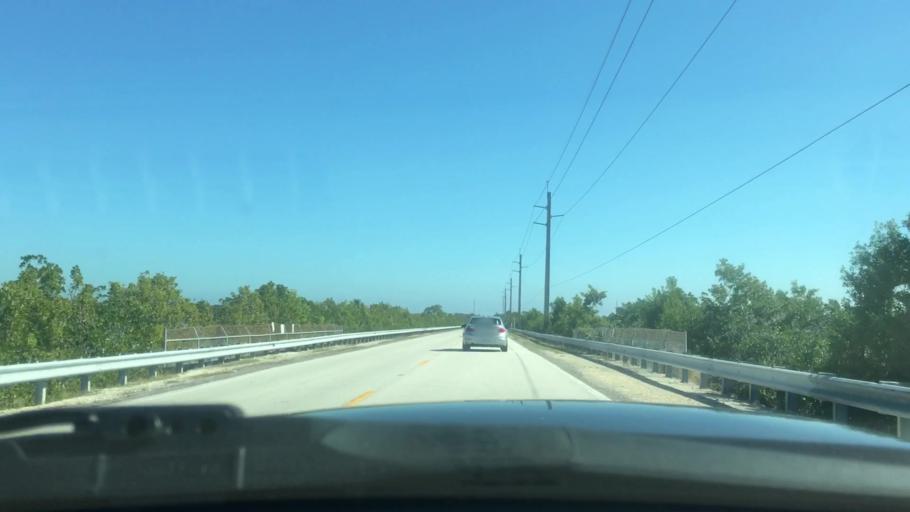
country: US
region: Florida
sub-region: Monroe County
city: North Key Largo
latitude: 25.2846
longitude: -80.3099
